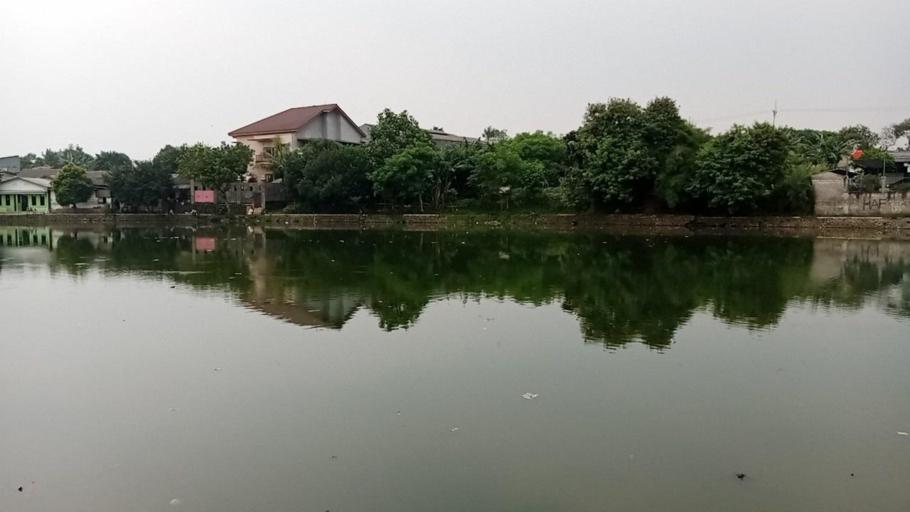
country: ID
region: West Java
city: Depok
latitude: -6.4461
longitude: 106.7998
